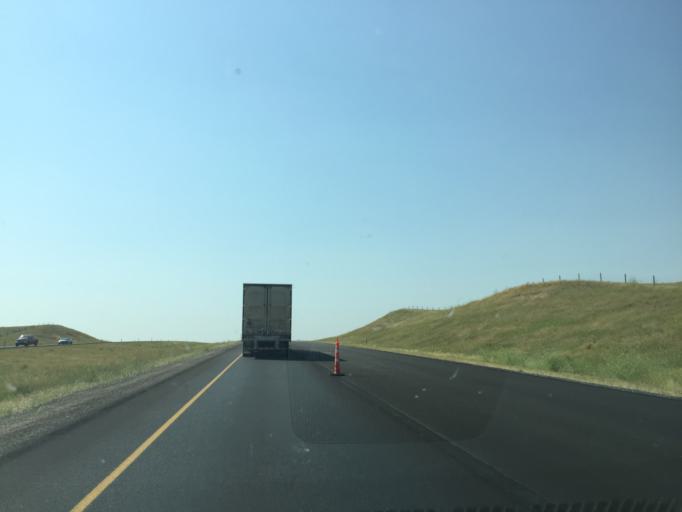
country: US
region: Wyoming
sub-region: Laramie County
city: Ranchettes
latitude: 41.3197
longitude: -104.8607
